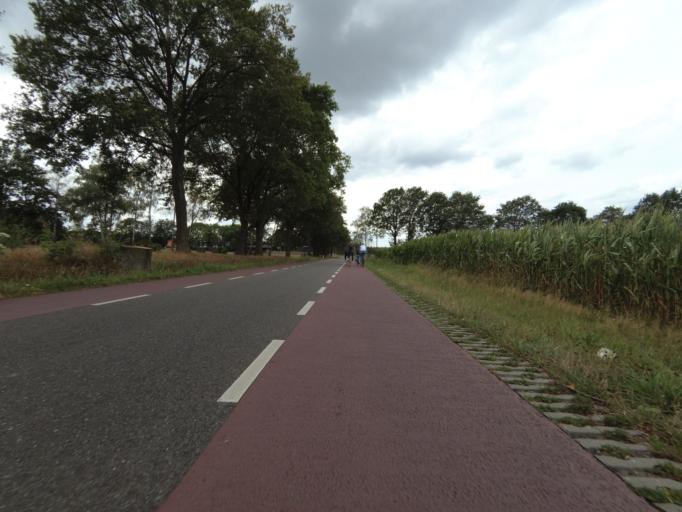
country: NL
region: Overijssel
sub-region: Gemeente Enschede
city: Enschede
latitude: 52.2634
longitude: 6.9032
